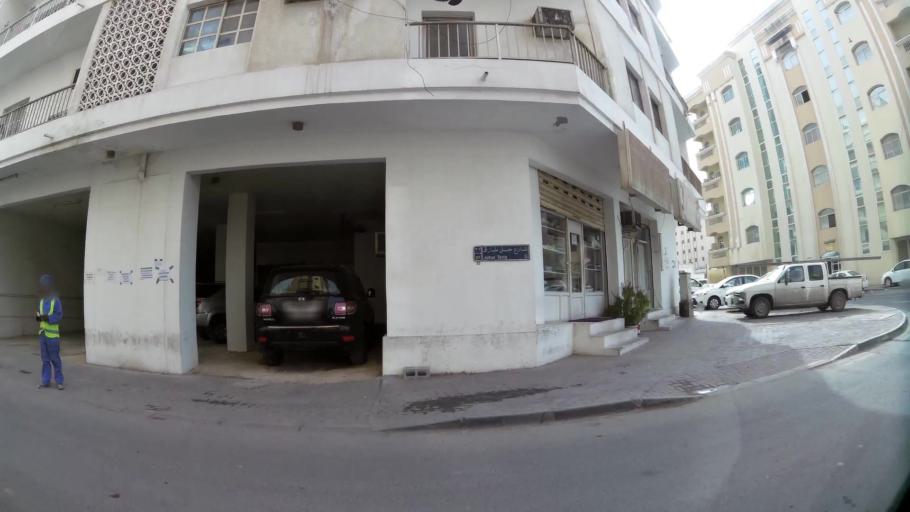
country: QA
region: Baladiyat ad Dawhah
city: Doha
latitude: 25.2810
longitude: 51.5487
